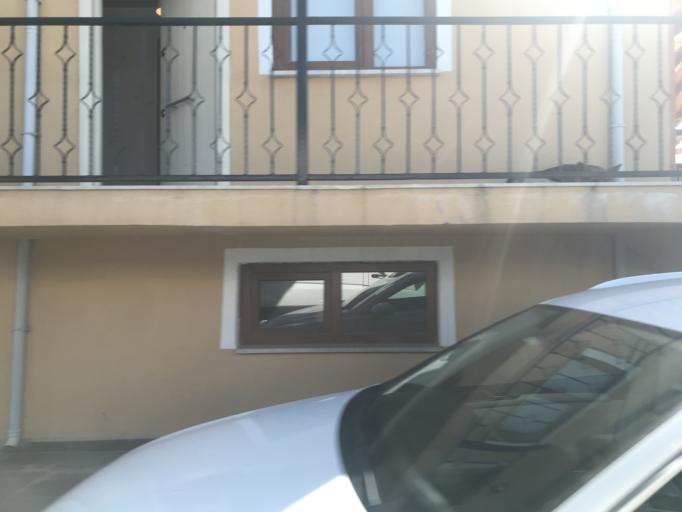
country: TR
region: Kirklareli
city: Kirklareli
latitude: 41.7876
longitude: 27.2349
